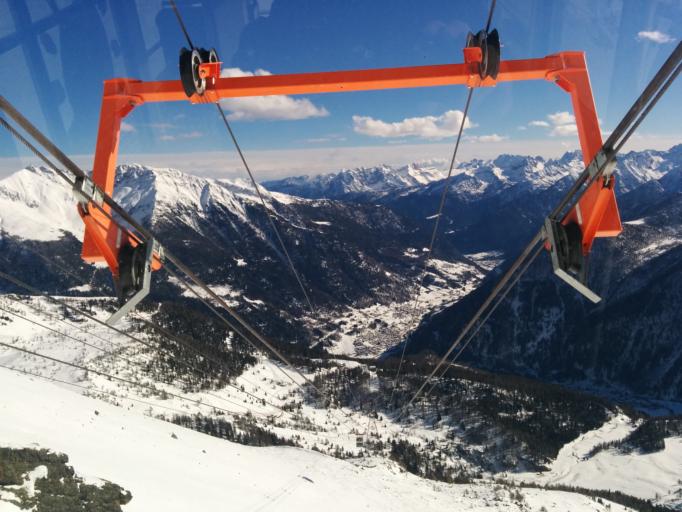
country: IT
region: Trentino-Alto Adige
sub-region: Provincia di Trento
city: Cogolo
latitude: 46.3796
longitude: 10.6394
